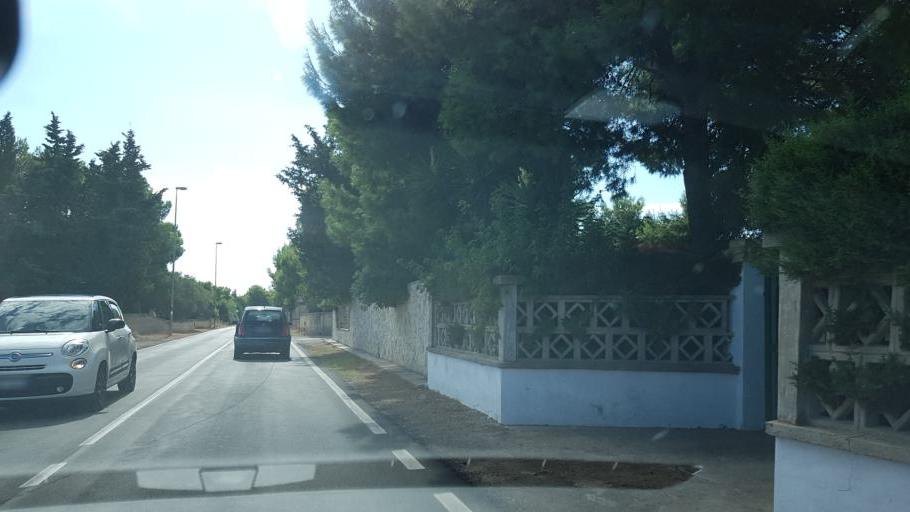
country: IT
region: Apulia
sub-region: Provincia di Lecce
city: Porto Cesareo
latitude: 40.2451
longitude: 17.9137
